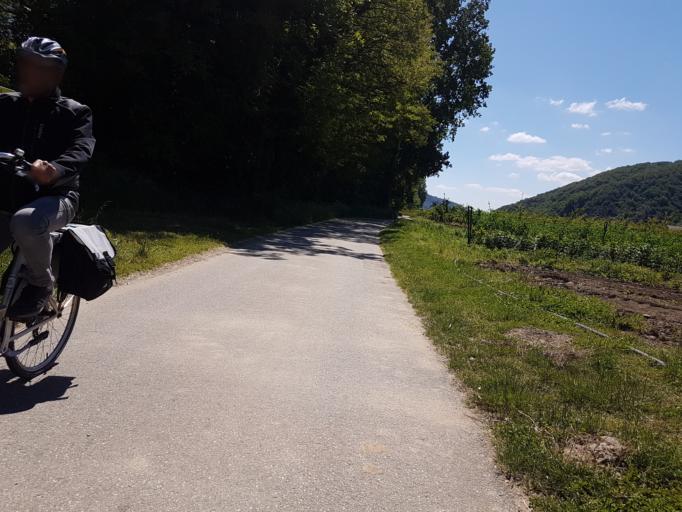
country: FR
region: Rhone-Alpes
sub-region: Departement de l'Ardeche
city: Saint-Jean-de-Muzols
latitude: 45.1157
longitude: 4.8083
